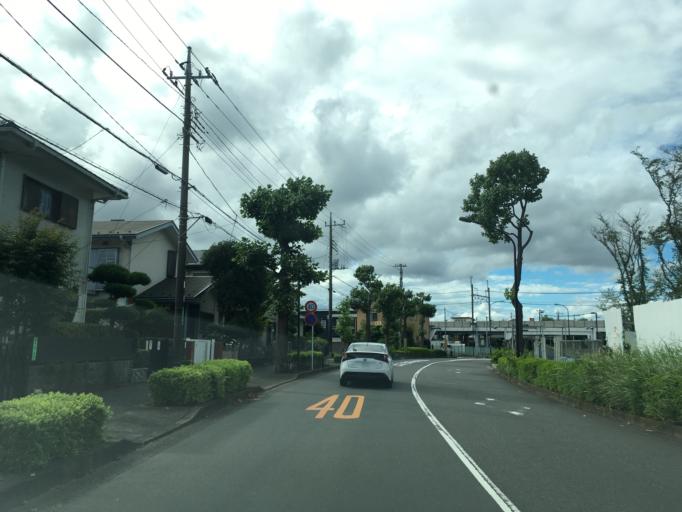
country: JP
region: Kanagawa
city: Minami-rinkan
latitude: 35.5101
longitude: 139.4665
